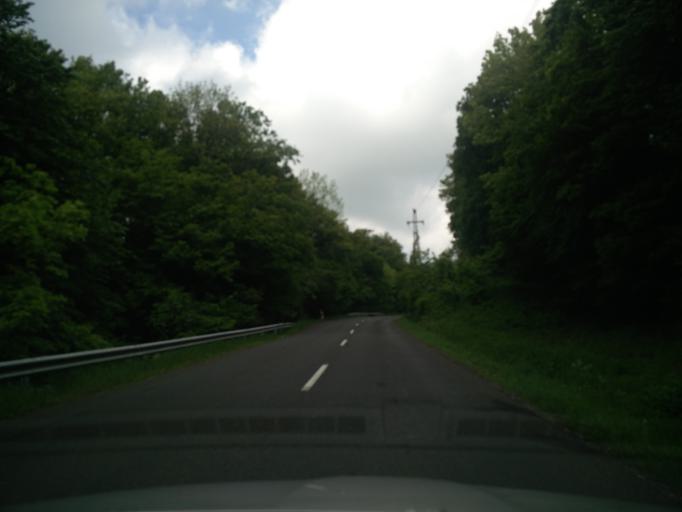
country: HU
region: Pest
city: Pilisszentkereszt
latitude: 47.7054
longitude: 18.8864
